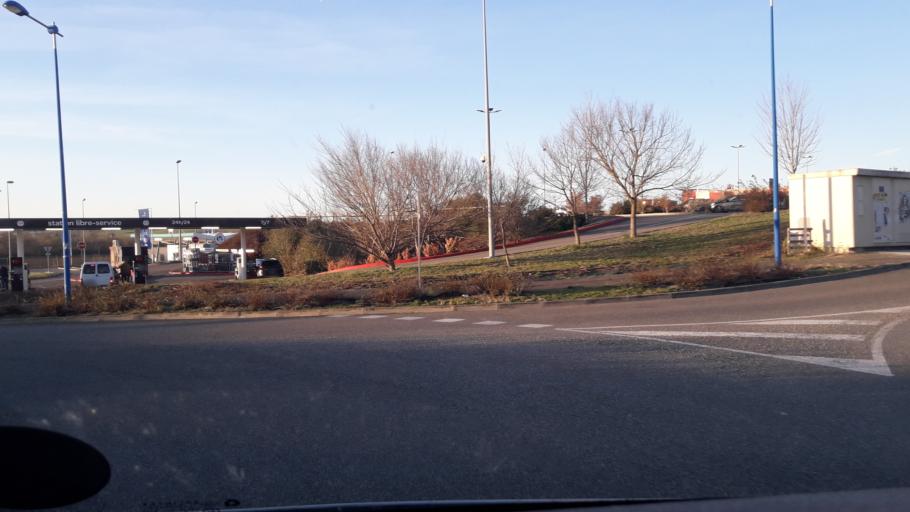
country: FR
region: Midi-Pyrenees
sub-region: Departement du Gers
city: Pujaudran
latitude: 43.6005
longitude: 1.0692
